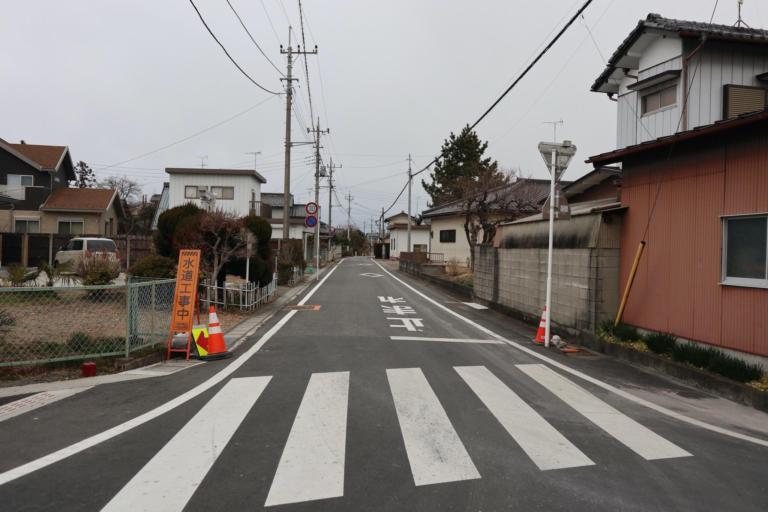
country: JP
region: Saitama
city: Hanyu
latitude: 36.2073
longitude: 139.5157
